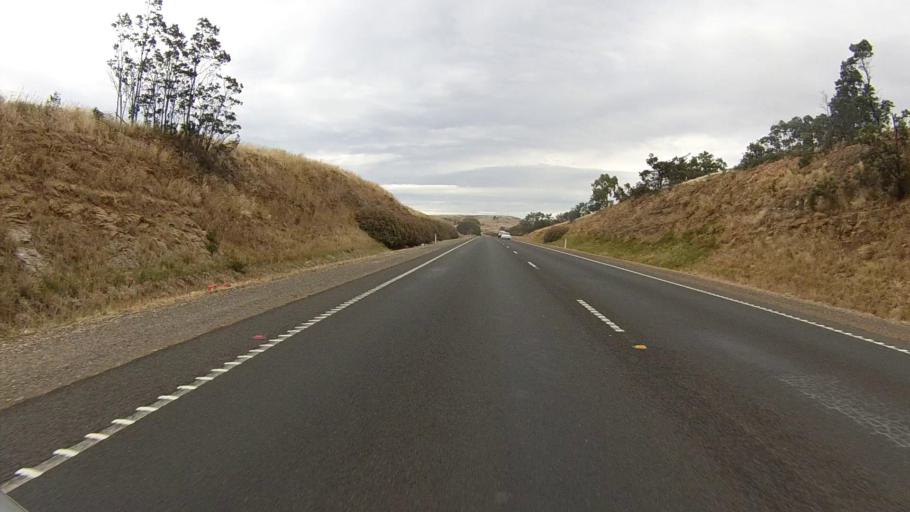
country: AU
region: Tasmania
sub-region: Brighton
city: Bridgewater
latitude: -42.3530
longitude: 147.3370
